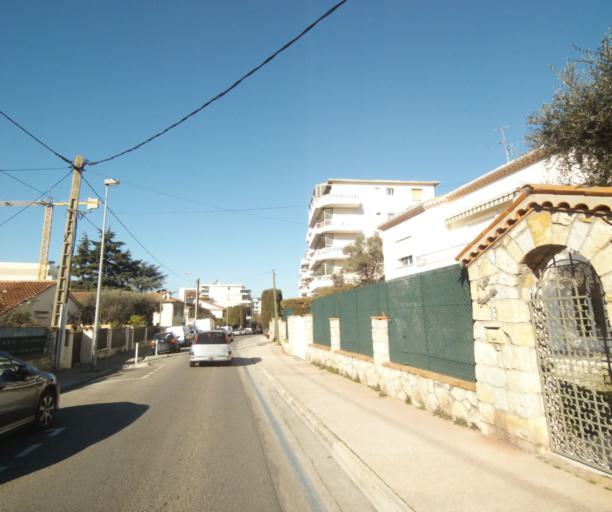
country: FR
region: Provence-Alpes-Cote d'Azur
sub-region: Departement des Alpes-Maritimes
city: Antibes
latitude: 43.5720
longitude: 7.1117
